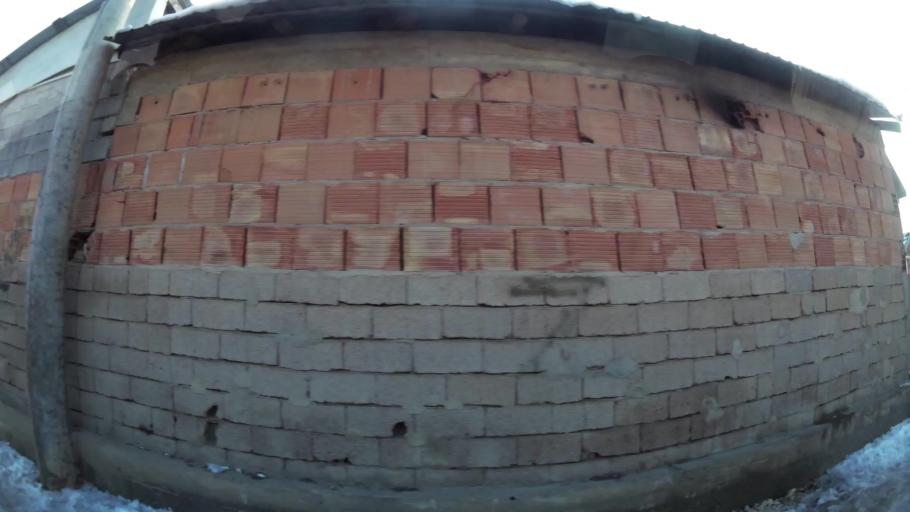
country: MK
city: Creshevo
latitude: 42.0198
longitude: 21.5113
